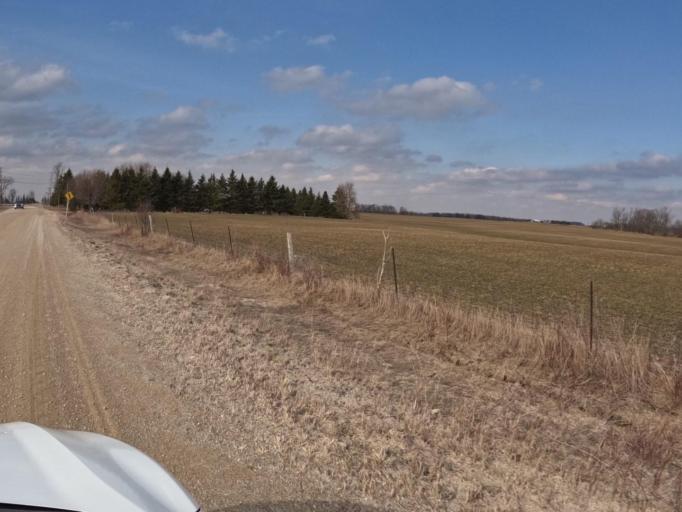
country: CA
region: Ontario
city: Shelburne
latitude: 43.9247
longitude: -80.3070
